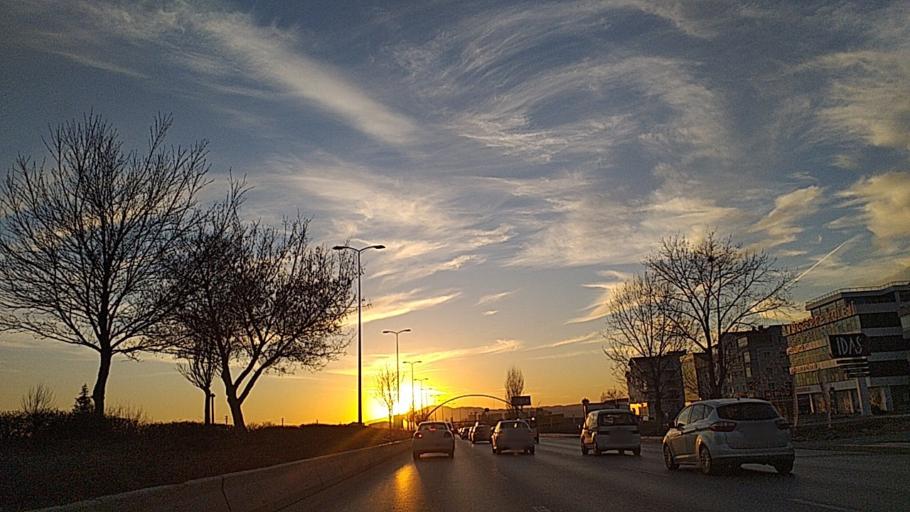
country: TR
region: Ankara
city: Etimesgut
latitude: 39.9629
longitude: 32.6618
